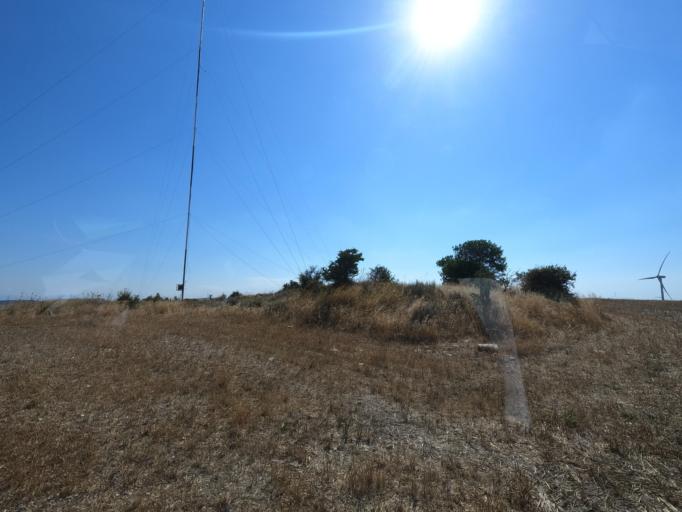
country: CY
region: Larnaka
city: Psevdas
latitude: 34.9694
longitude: 33.4837
